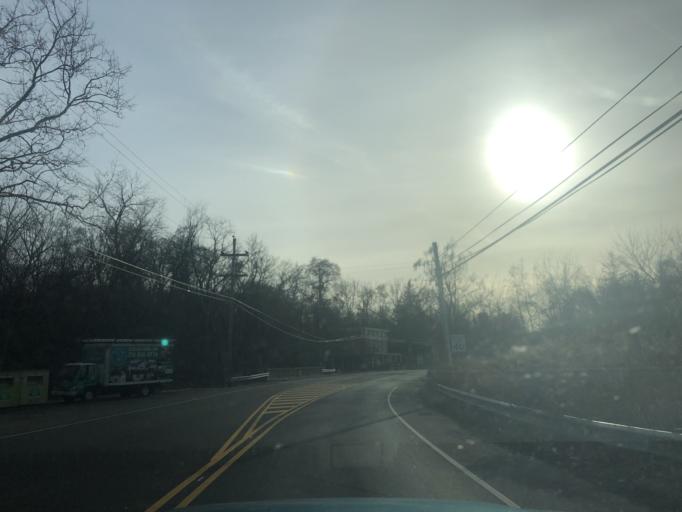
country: US
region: Pennsylvania
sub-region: Montgomery County
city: Fort Washington
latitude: 40.1342
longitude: -75.2137
